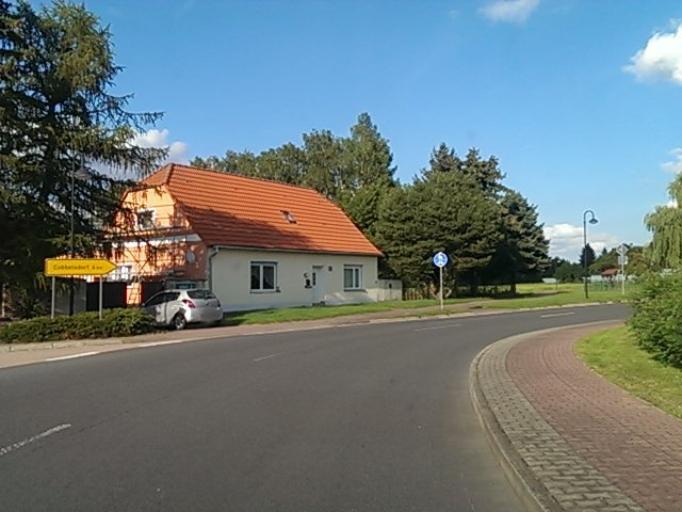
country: DE
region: Saxony-Anhalt
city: Coswig
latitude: 51.9578
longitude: 12.4821
